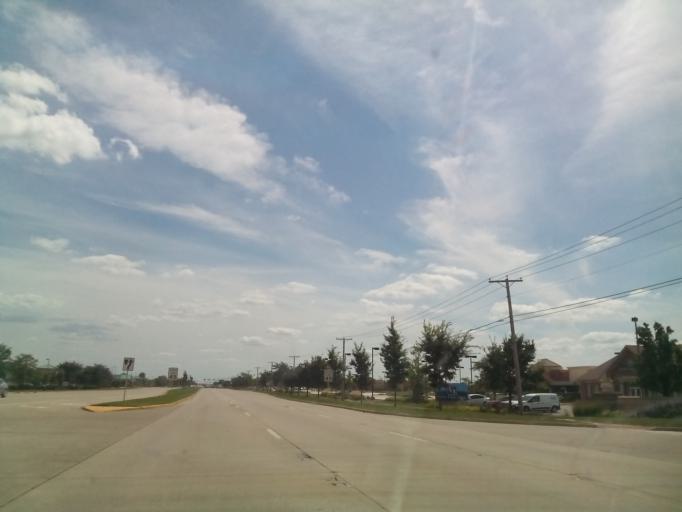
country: US
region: Illinois
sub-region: Will County
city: Plainfield
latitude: 41.7172
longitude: -88.2061
